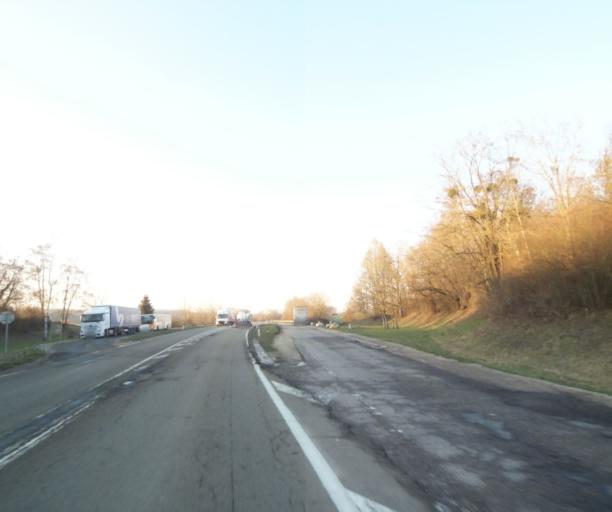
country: FR
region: Champagne-Ardenne
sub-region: Departement de la Haute-Marne
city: Bienville
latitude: 48.5799
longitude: 5.0308
